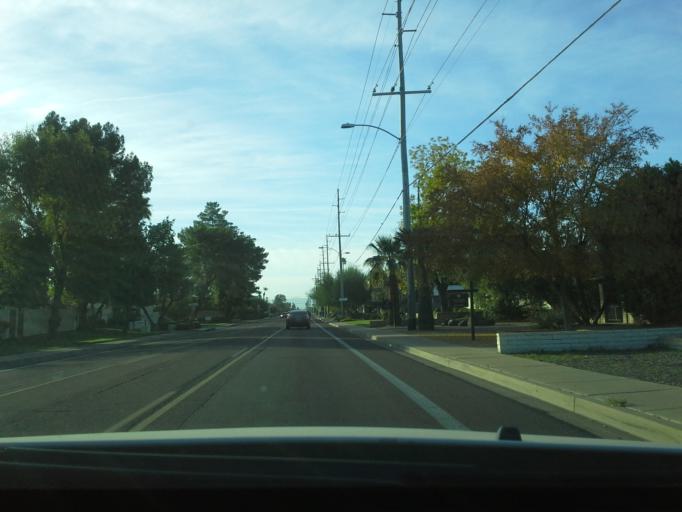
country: US
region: Arizona
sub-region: Maricopa County
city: Phoenix
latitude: 33.5197
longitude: -112.0563
